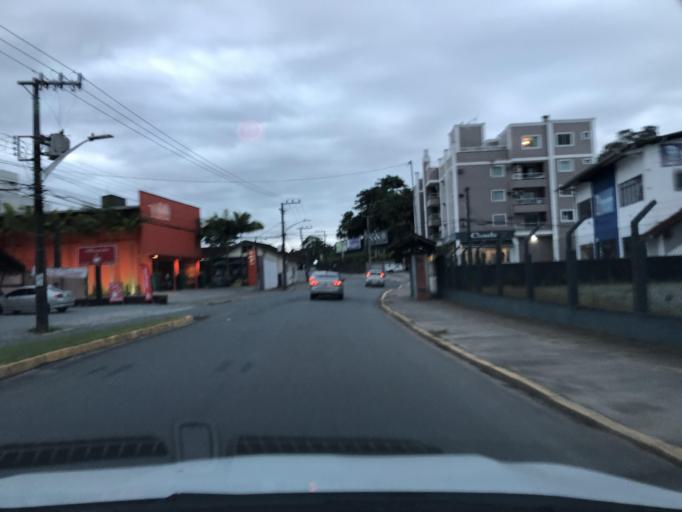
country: BR
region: Santa Catarina
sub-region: Joinville
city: Joinville
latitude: -26.2962
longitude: -48.8681
